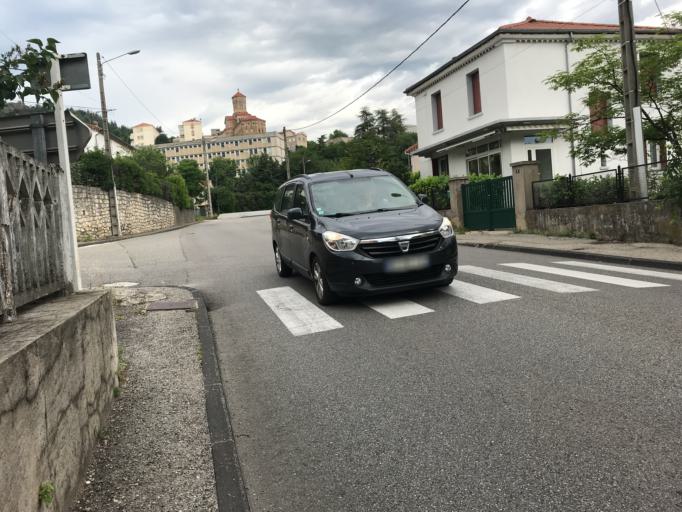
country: FR
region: Rhone-Alpes
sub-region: Departement de l'Ardeche
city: Privas
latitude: 44.7295
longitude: 4.5971
